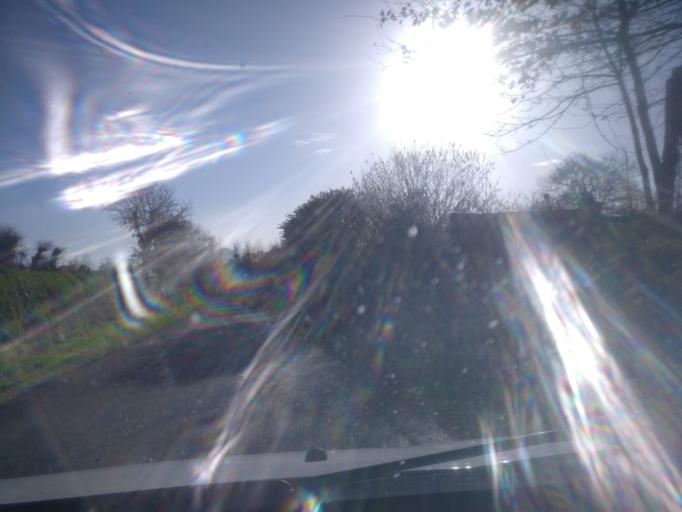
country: FR
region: Brittany
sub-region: Departement d'Ille-et-Vilaine
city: Pleine-Fougeres
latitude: 48.5317
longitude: -1.5362
